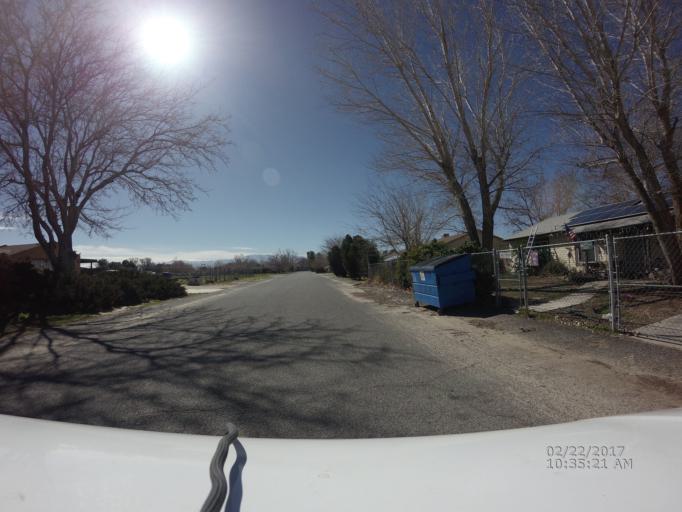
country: US
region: California
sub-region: Los Angeles County
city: Lake Los Angeles
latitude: 34.6276
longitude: -117.8216
